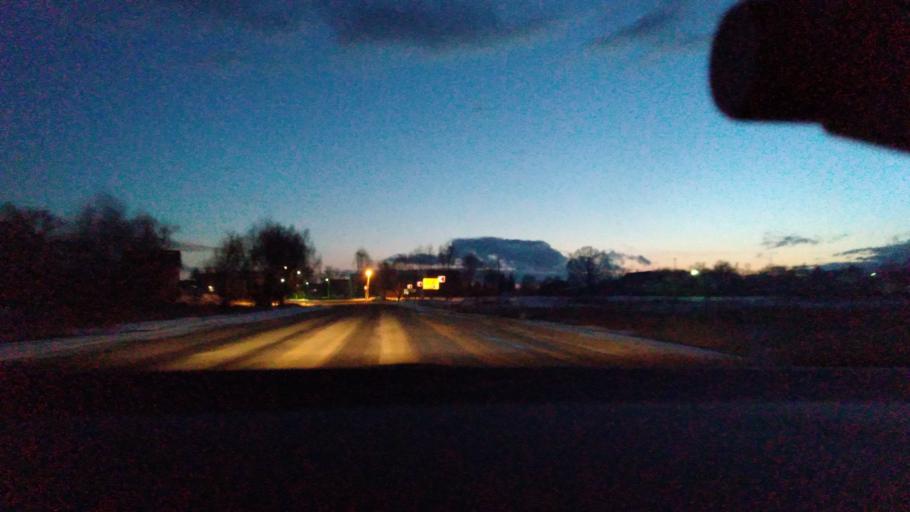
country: RU
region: Moskovskaya
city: Krasnaya Poyma
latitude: 55.0602
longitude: 39.1148
